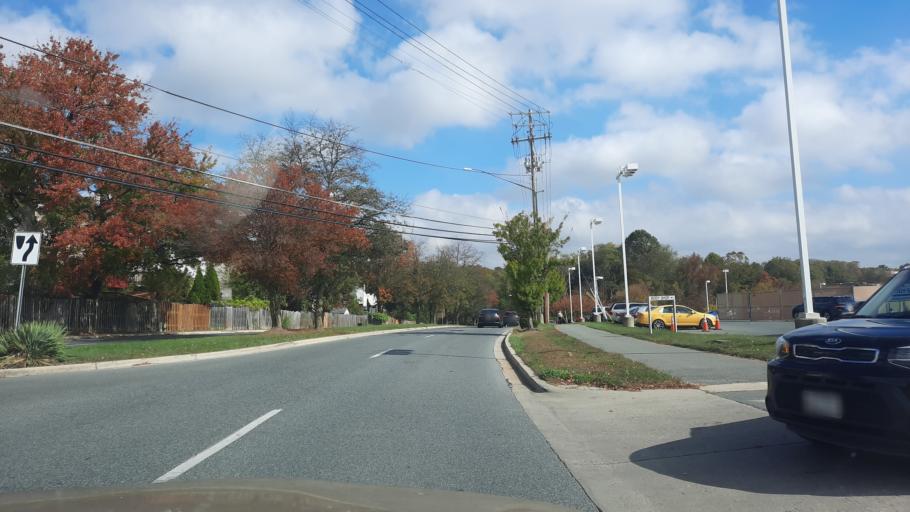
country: US
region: Maryland
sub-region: Montgomery County
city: Gaithersburg
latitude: 39.1597
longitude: -77.2179
